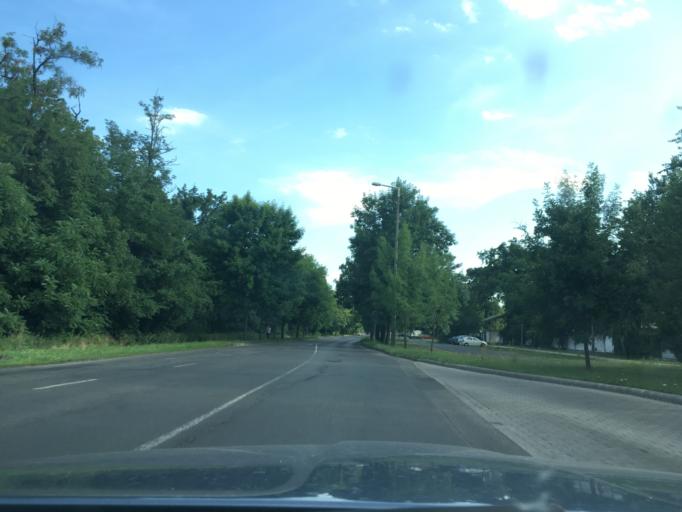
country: HU
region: Hajdu-Bihar
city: Debrecen
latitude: 47.5610
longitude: 21.6306
